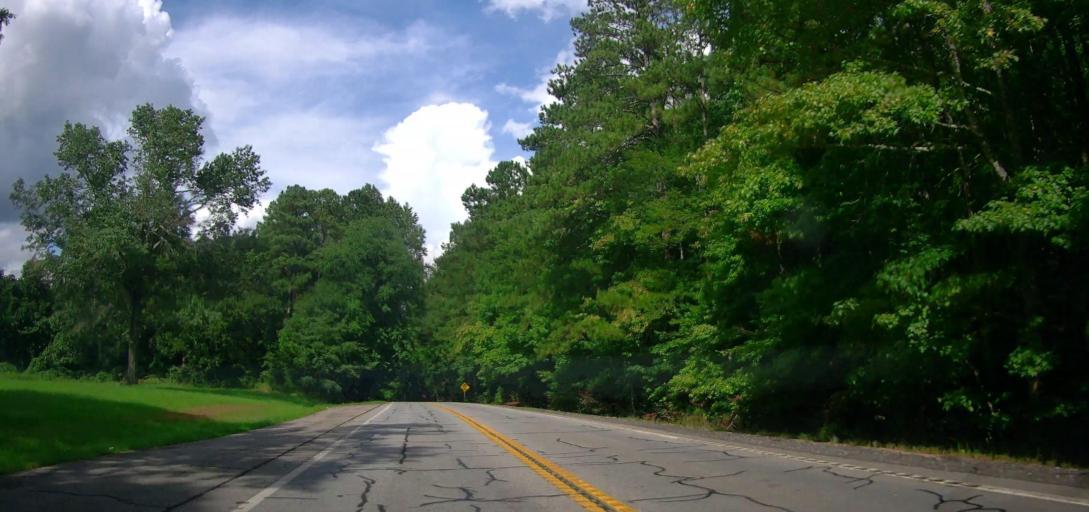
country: US
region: Georgia
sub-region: Harris County
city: Pine Mountain
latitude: 32.8211
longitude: -84.8454
